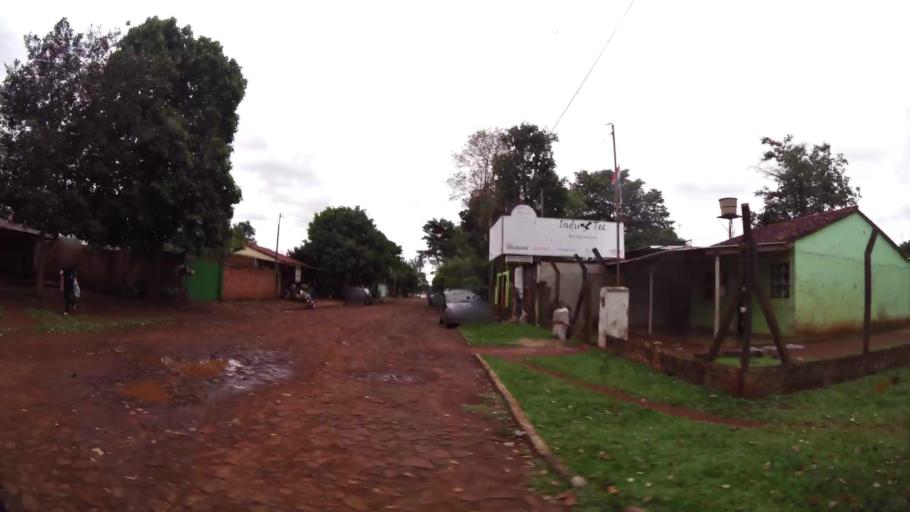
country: PY
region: Alto Parana
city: Ciudad del Este
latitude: -25.4013
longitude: -54.6284
